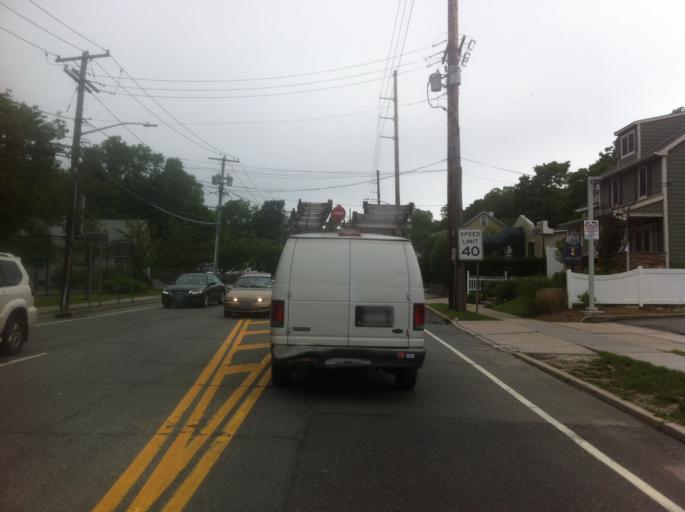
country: US
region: New York
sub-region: Nassau County
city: Oyster Bay
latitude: 40.8653
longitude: -73.5326
